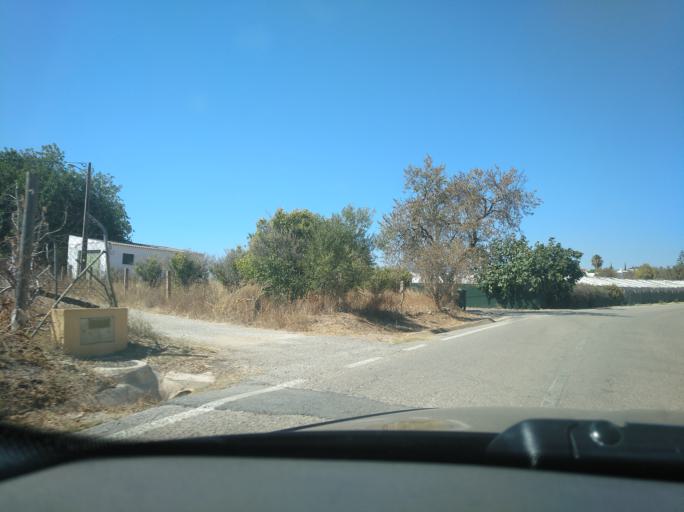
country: PT
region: Faro
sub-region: Faro
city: Faro
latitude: 37.0619
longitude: -7.8986
